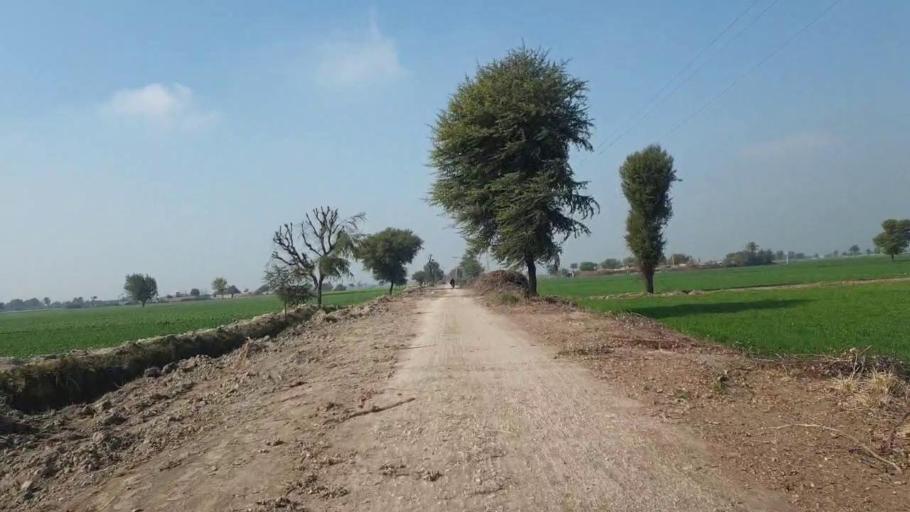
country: PK
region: Sindh
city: Shahdadpur
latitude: 26.0238
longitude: 68.5811
